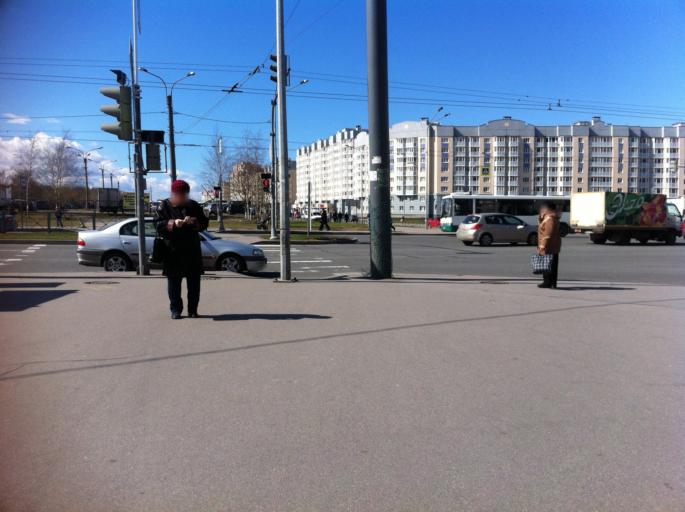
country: RU
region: St.-Petersburg
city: Uritsk
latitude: 59.8572
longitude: 30.1768
